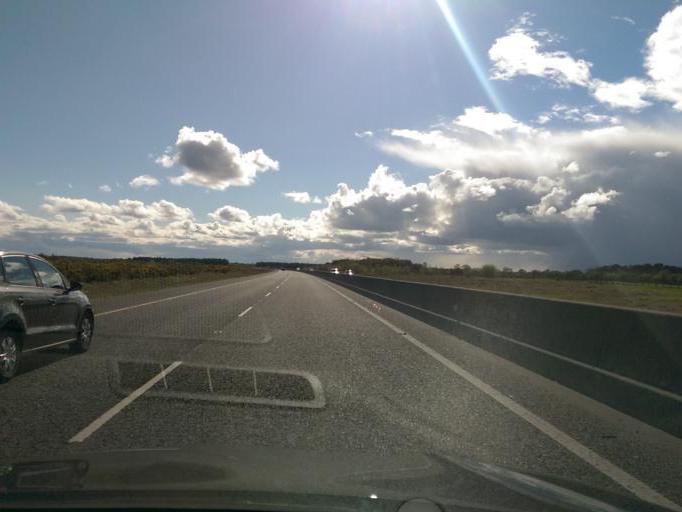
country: IE
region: Leinster
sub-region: An Iarmhi
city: Rochfortbridge
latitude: 53.4221
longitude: -7.2439
